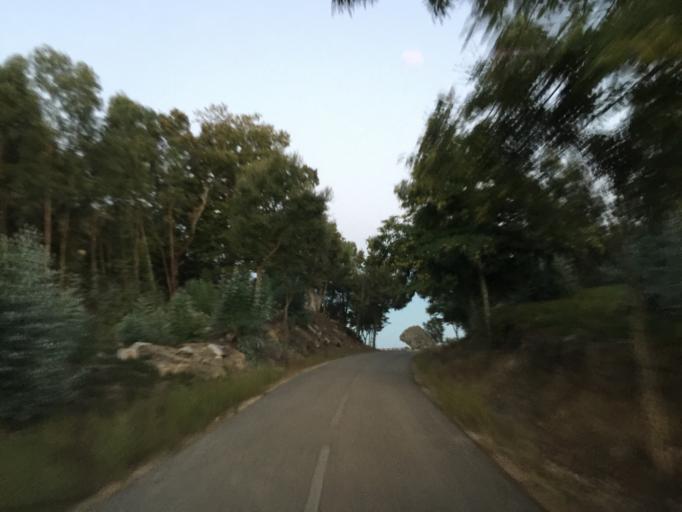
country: PT
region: Portalegre
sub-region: Castelo de Vide
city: Castelo de Vide
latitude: 39.4040
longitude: -7.4563
